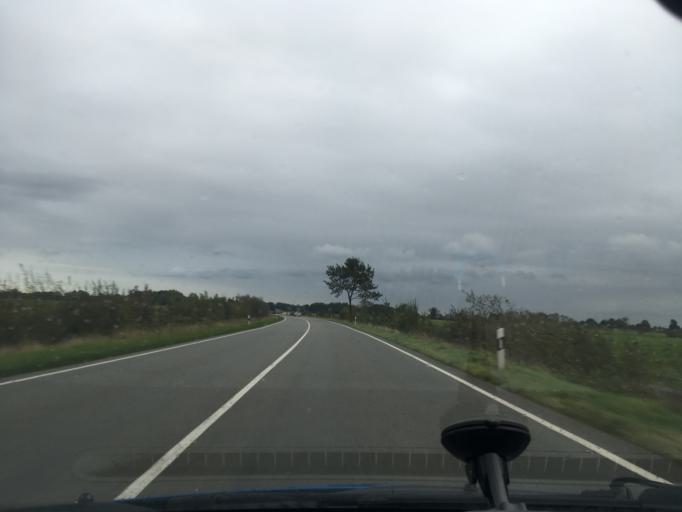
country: DE
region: Lower Saxony
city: Handorf
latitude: 53.3933
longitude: 10.3341
